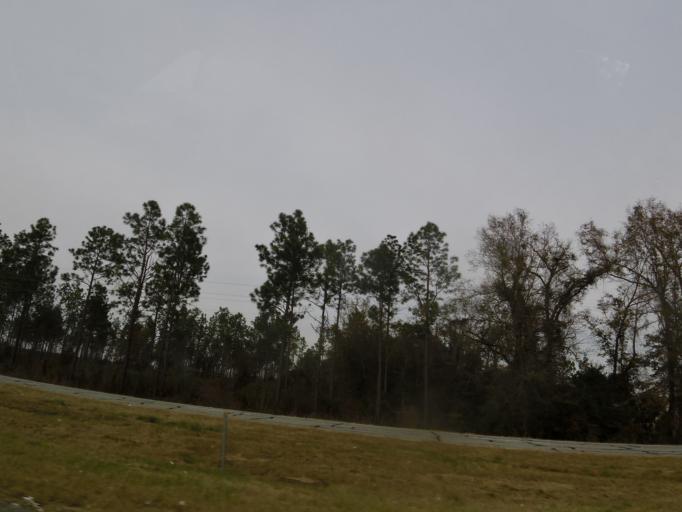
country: US
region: Georgia
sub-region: Decatur County
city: Bainbridge
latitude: 30.9451
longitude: -84.6950
